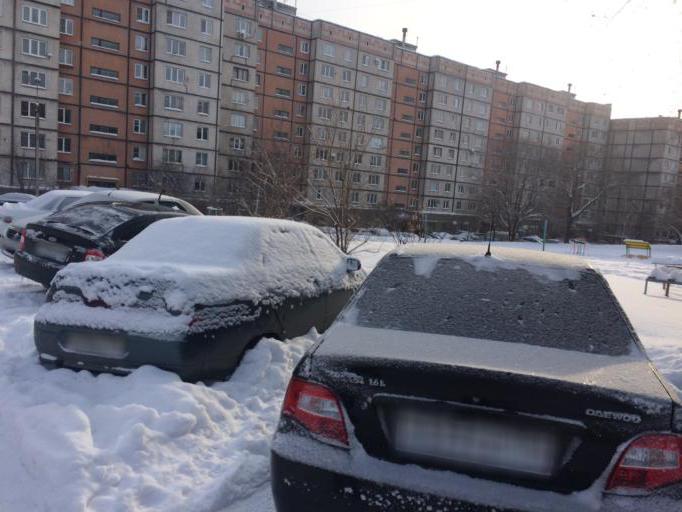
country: RU
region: Chelyabinsk
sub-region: Gorod Magnitogorsk
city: Magnitogorsk
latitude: 53.4045
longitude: 58.9836
